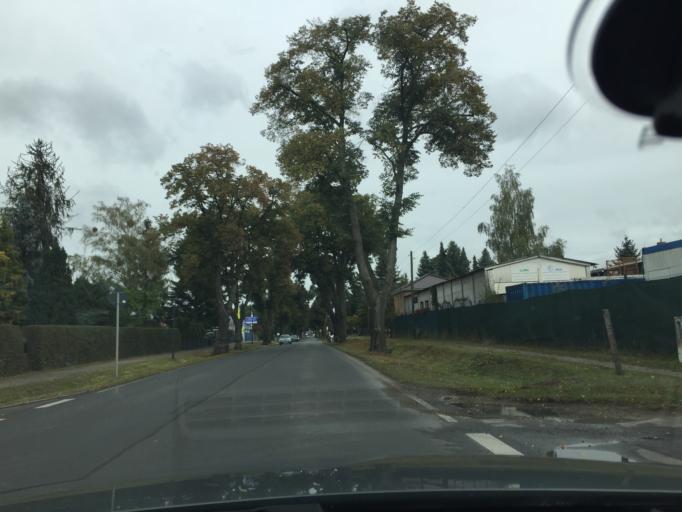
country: DE
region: Berlin
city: Hellersdorf
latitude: 52.5307
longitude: 13.6275
